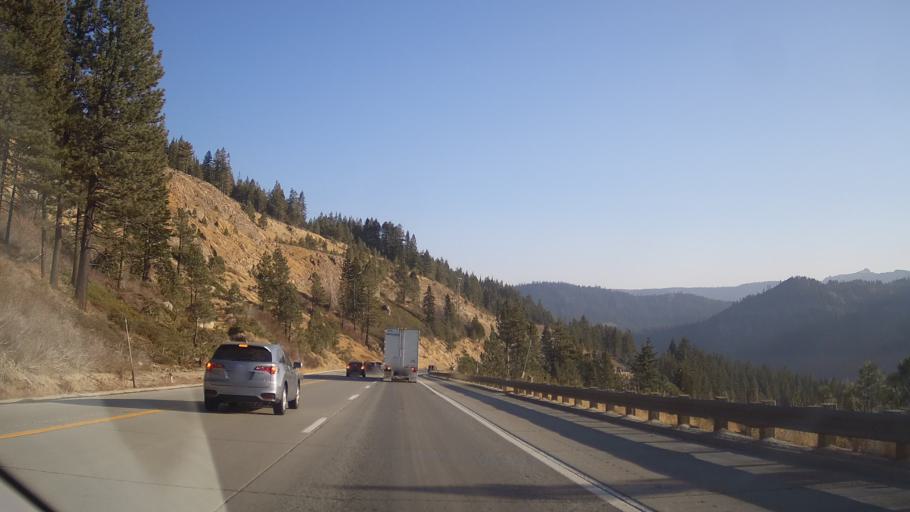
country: US
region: California
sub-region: Nevada County
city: Truckee
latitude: 39.3389
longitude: -120.3092
